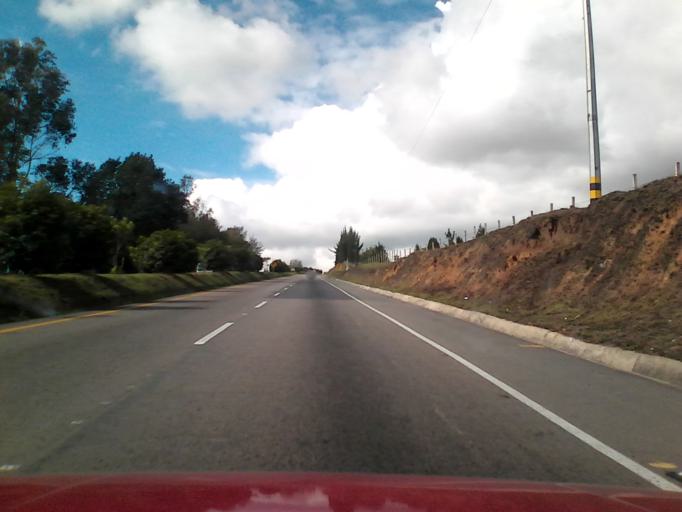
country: CO
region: Boyaca
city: Combita
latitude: 5.6320
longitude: -73.2975
